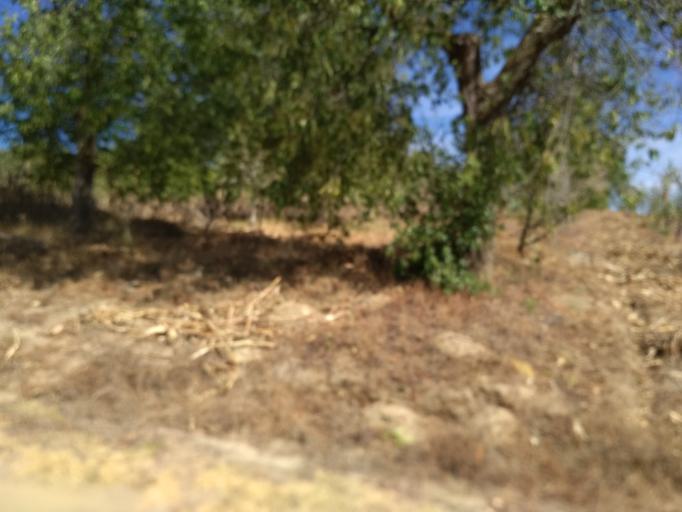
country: MX
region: Puebla
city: Domingo Arenas
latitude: 19.1242
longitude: -98.5005
